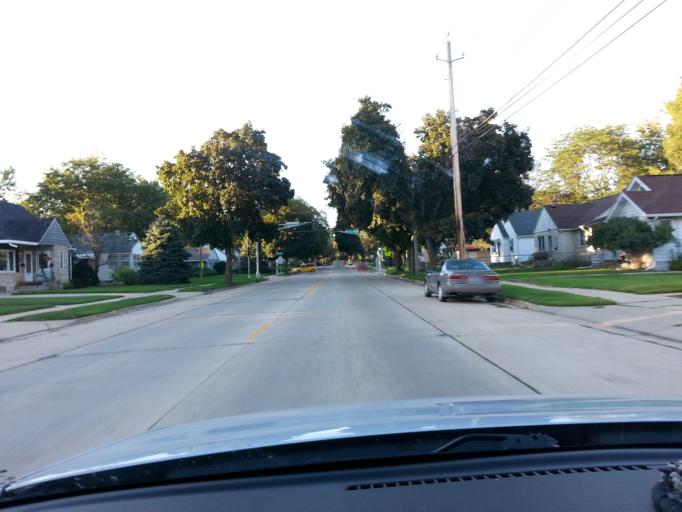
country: US
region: Minnesota
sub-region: Olmsted County
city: Rochester
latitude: 44.0336
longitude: -92.4488
